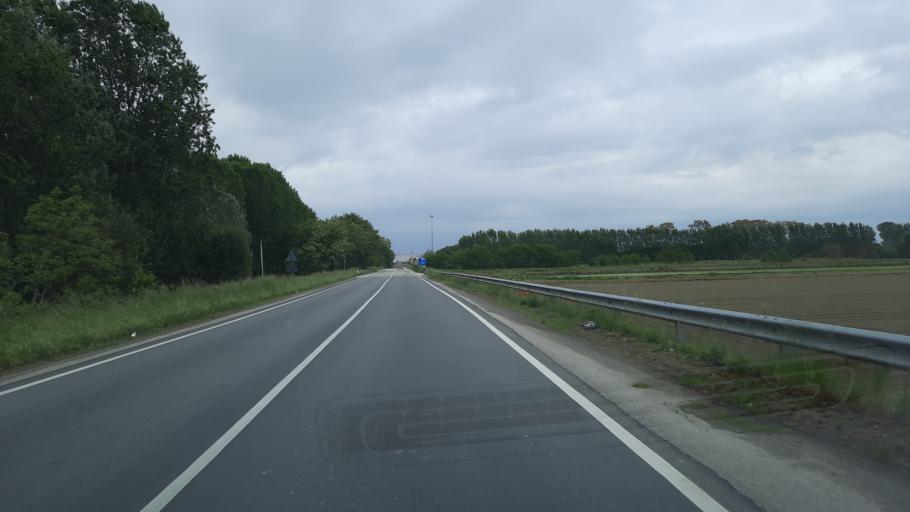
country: IT
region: Lombardy
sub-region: Provincia di Pavia
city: Robbio
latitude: 45.2895
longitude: 8.5726
